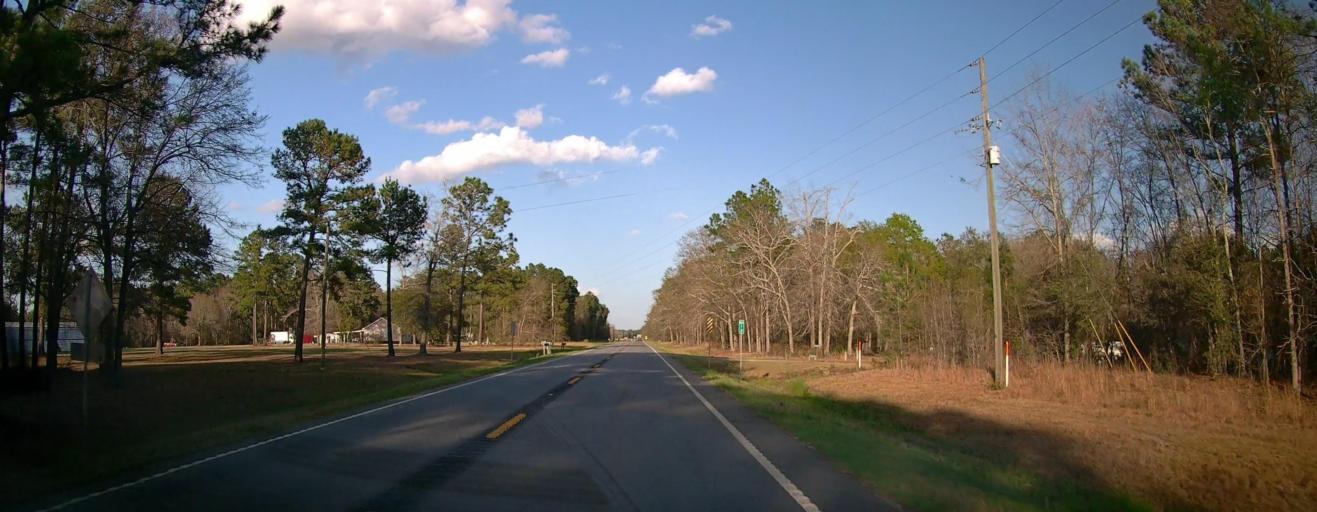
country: US
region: Georgia
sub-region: Tattnall County
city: Reidsville
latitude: 32.1413
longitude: -82.0322
